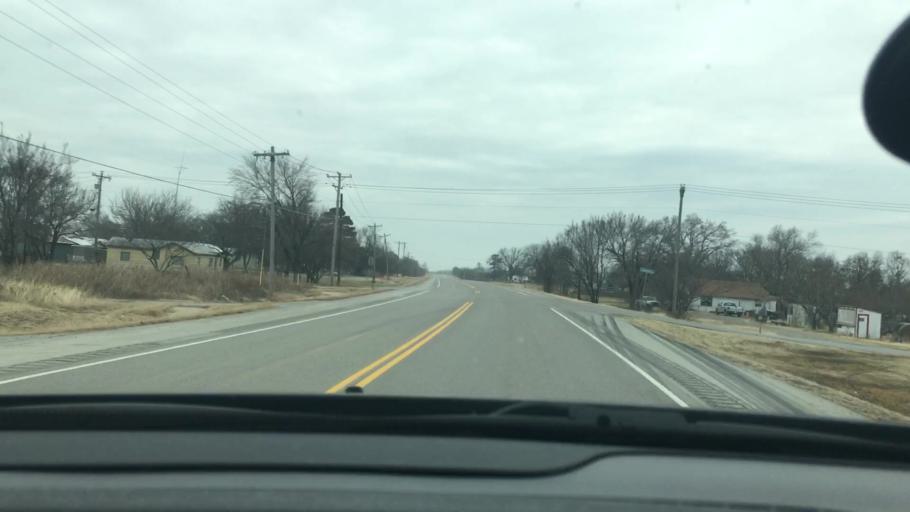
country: US
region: Oklahoma
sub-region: Carter County
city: Healdton
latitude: 34.4057
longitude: -97.5092
